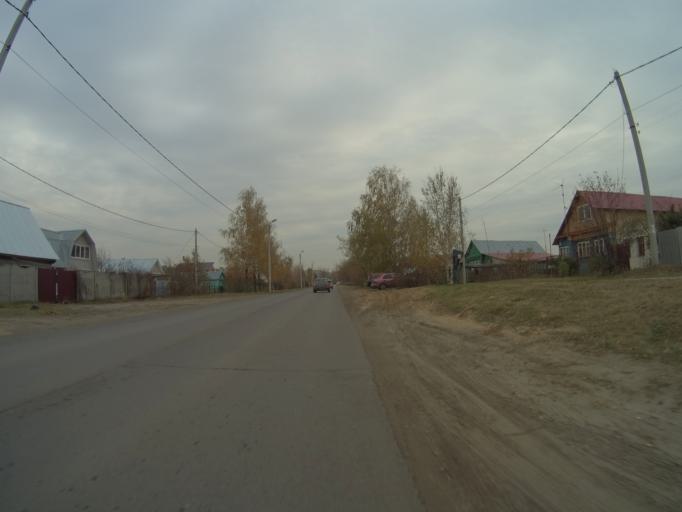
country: RU
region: Vladimir
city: Kommunar
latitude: 56.1108
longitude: 40.4469
